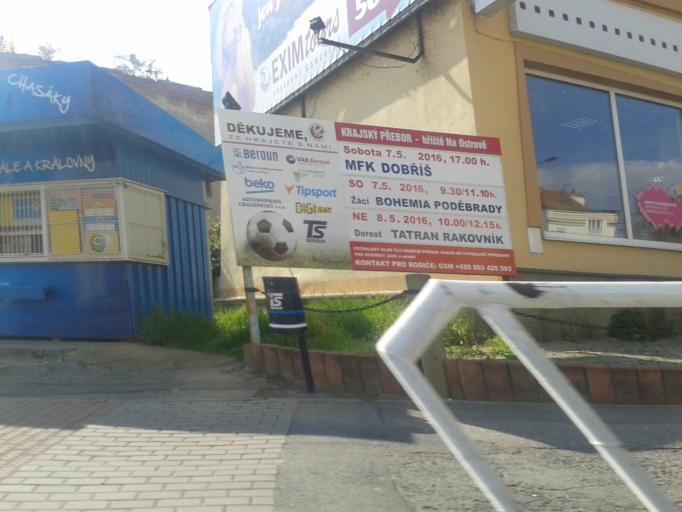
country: CZ
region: Central Bohemia
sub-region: Okres Beroun
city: Beroun
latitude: 49.9632
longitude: 14.0703
